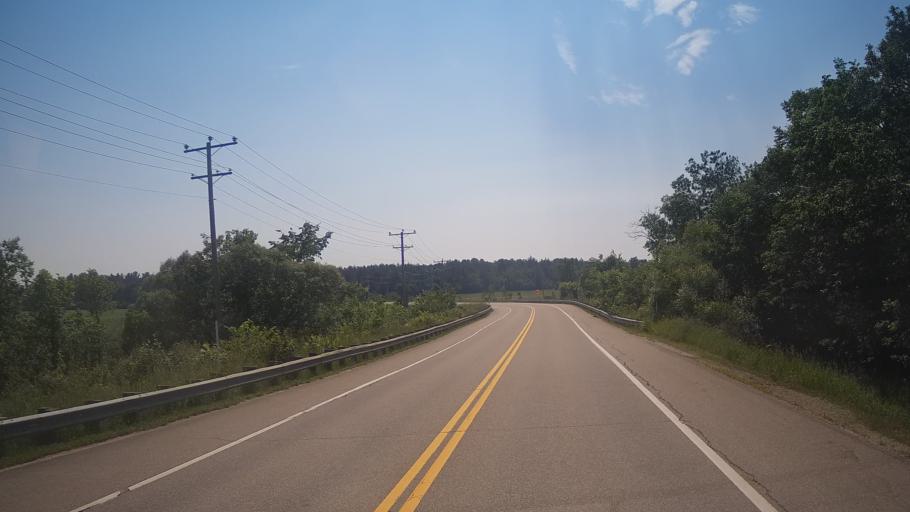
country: CA
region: Ontario
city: Pembroke
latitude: 45.8504
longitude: -77.0085
